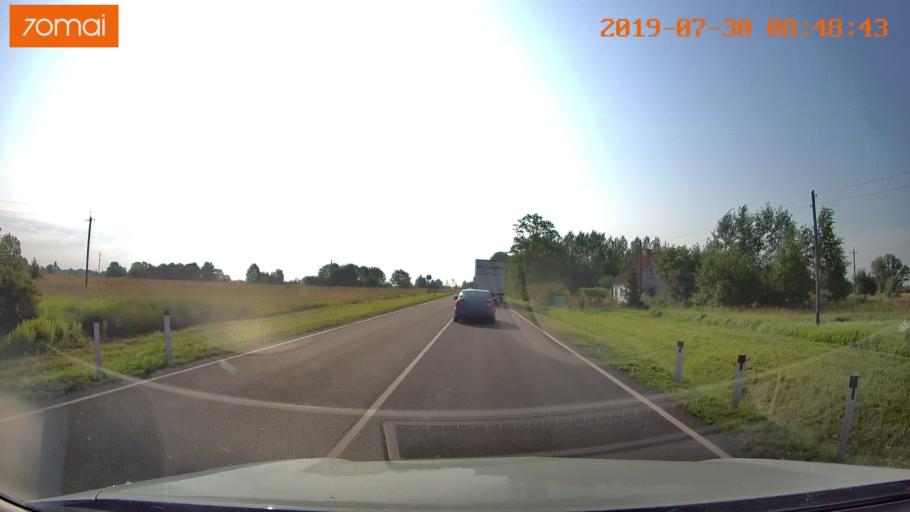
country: RU
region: Kaliningrad
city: Chernyakhovsk
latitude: 54.6160
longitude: 21.9098
